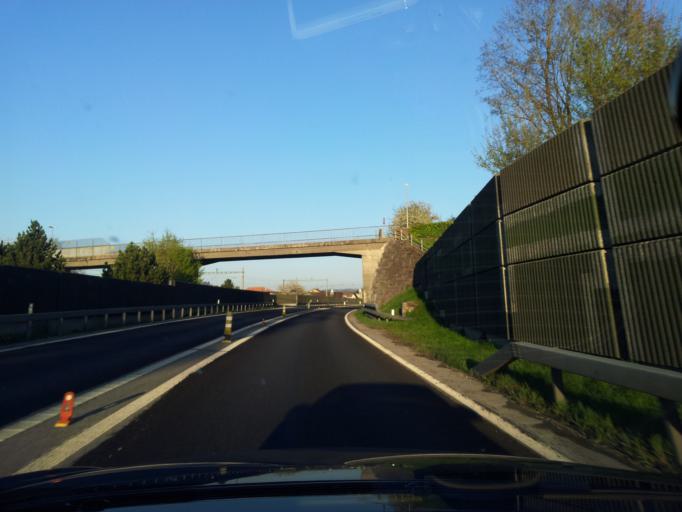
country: CH
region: Bern
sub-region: Biel/Bienne District
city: Brugg
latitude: 47.1177
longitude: 7.2886
